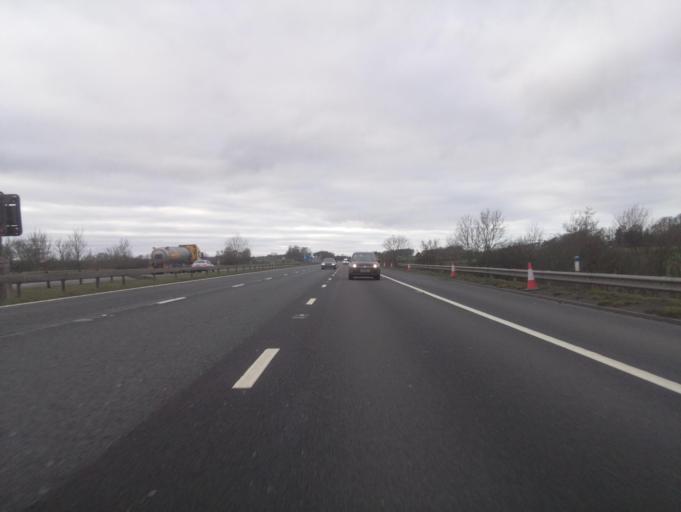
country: GB
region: England
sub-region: Cumbria
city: Carlisle
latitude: 54.9310
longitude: -2.9319
